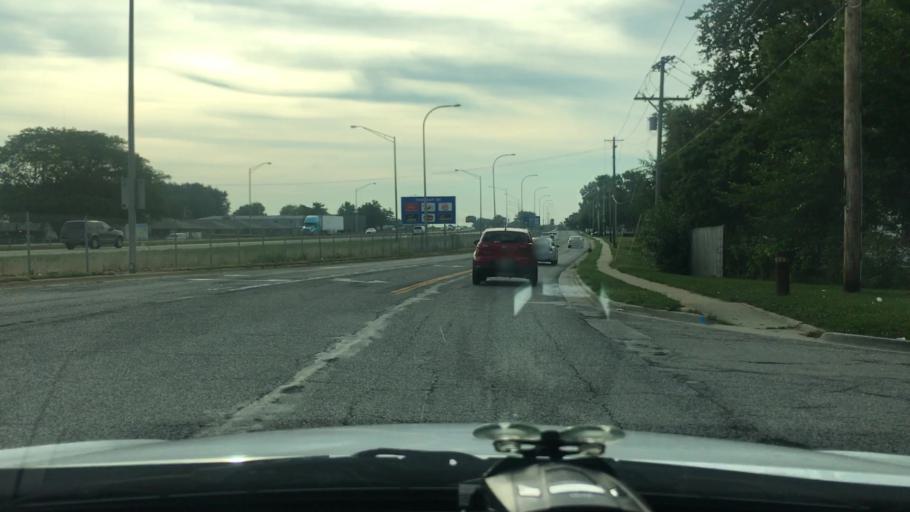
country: US
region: Illinois
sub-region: Champaign County
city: Champaign
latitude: 40.1391
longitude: -88.2748
